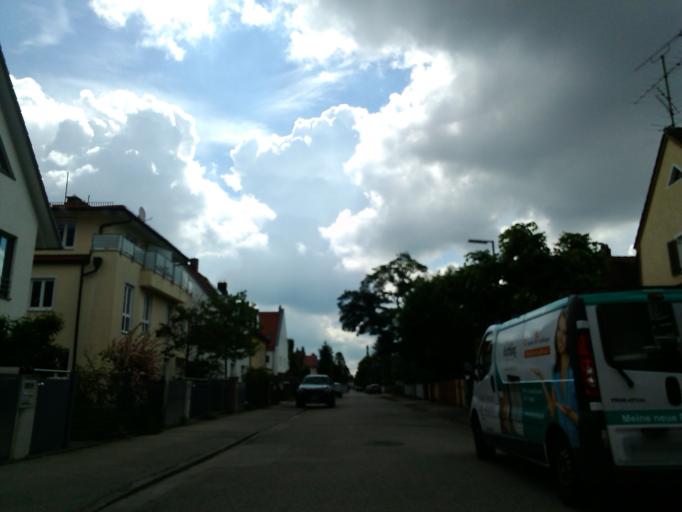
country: DE
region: Bavaria
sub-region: Upper Bavaria
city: Bogenhausen
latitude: 48.1225
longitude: 11.6478
